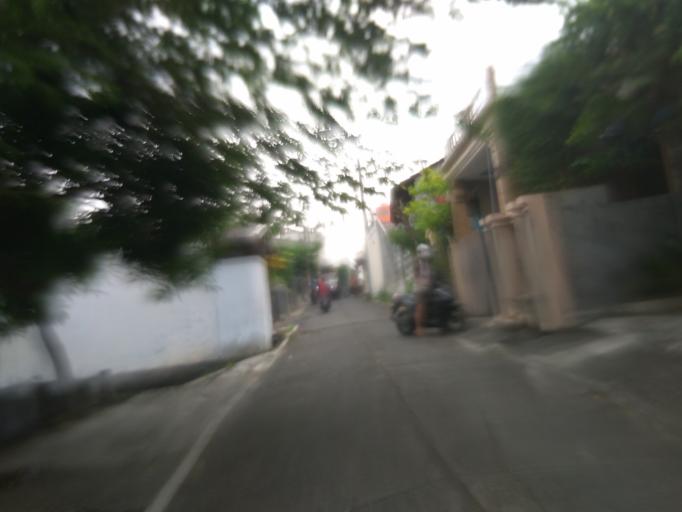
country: ID
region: Central Java
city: Semarang
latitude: -7.0107
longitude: 110.4111
